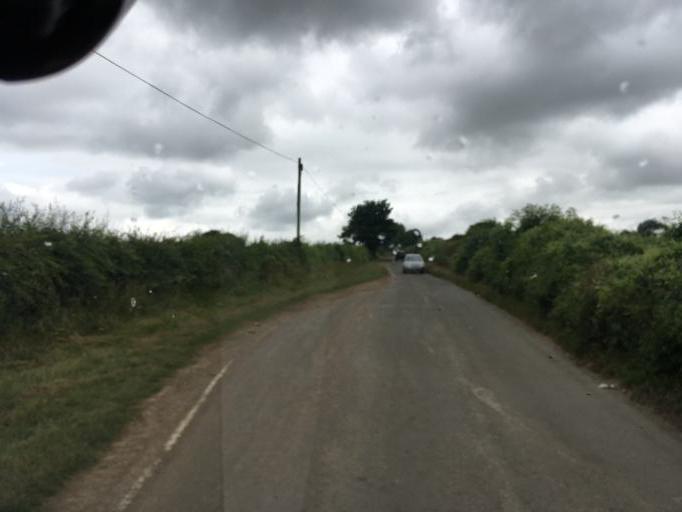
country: GB
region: England
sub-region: Gloucestershire
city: Nailsworth
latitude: 51.7001
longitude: -2.2493
